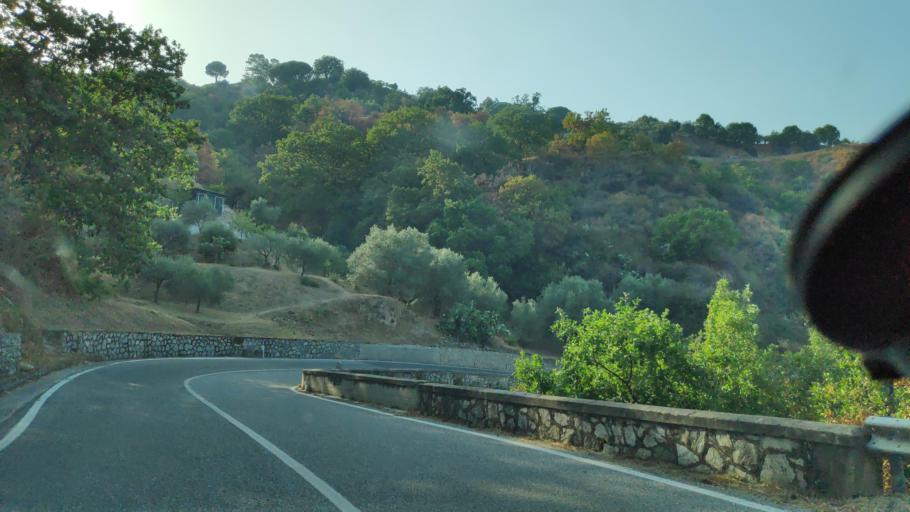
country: IT
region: Calabria
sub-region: Provincia di Catanzaro
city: Sant'Andrea Apostolo dello Ionio
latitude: 38.6175
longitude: 16.5350
